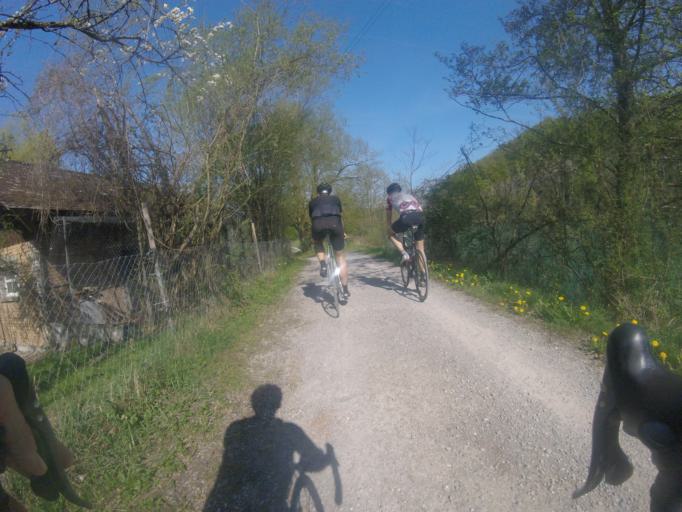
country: CH
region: Bern
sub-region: Bern-Mittelland District
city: Muhleberg
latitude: 46.9731
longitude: 7.2604
